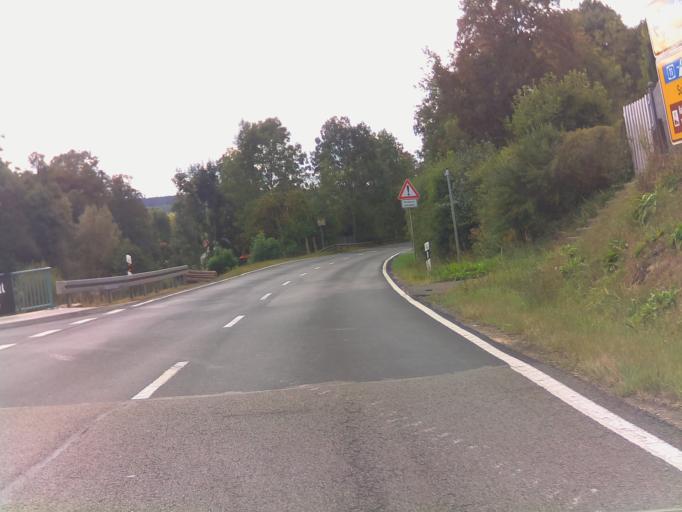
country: DE
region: Thuringia
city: Dillstadt
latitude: 50.5882
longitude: 10.5433
